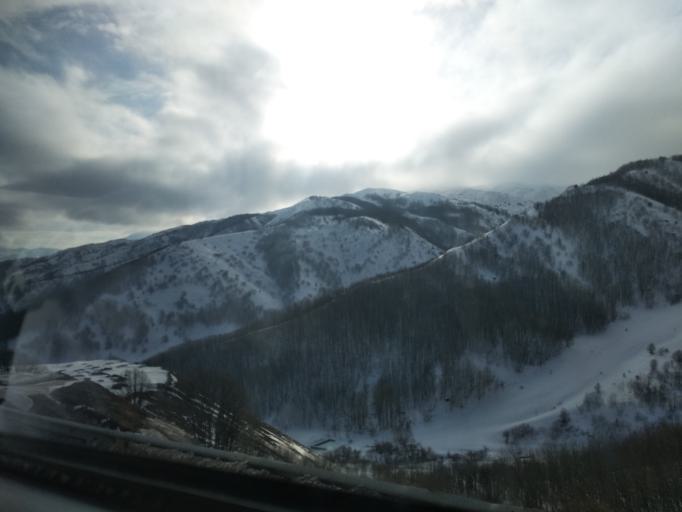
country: TR
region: Erzincan
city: Catalarmut
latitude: 39.8973
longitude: 39.3904
